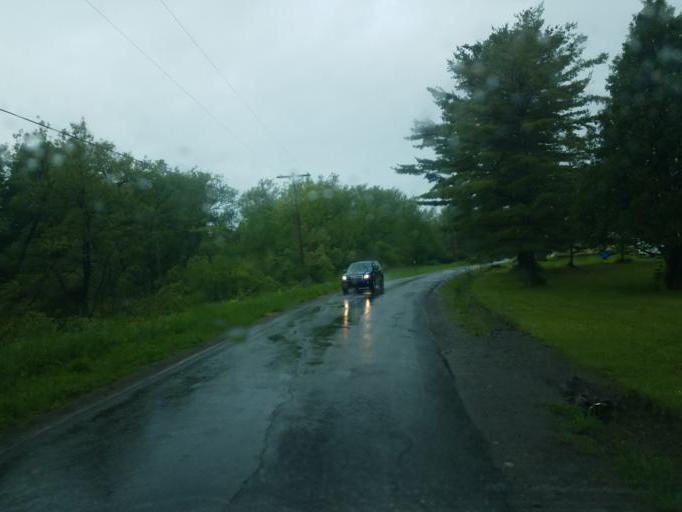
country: US
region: New York
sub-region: Herkimer County
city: Ilion
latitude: 42.9657
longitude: -75.0387
